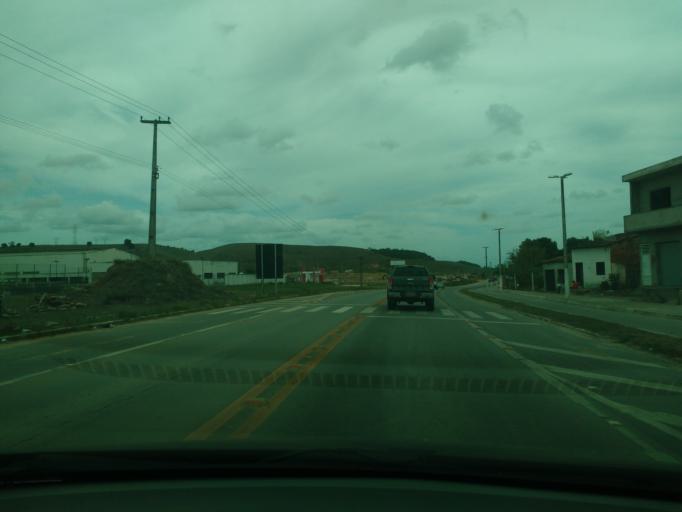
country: BR
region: Alagoas
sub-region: Murici
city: Murici
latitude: -9.3088
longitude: -35.9372
